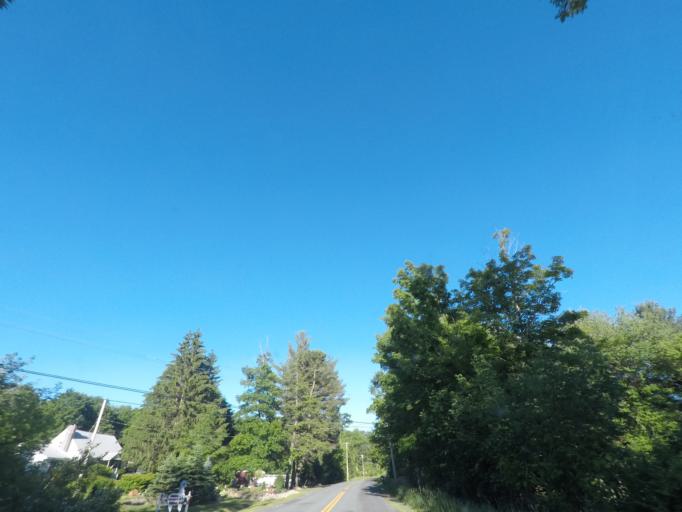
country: US
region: New York
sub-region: Rensselaer County
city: Averill Park
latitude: 42.5791
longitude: -73.5422
